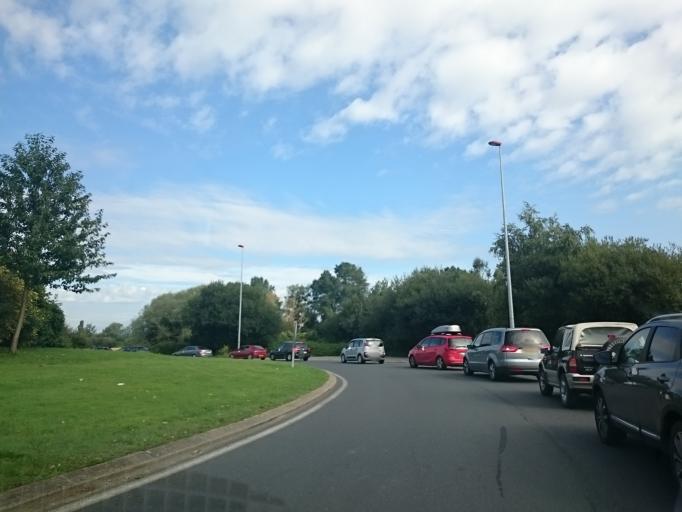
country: FR
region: Lower Normandy
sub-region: Departement de la Manche
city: Avranches
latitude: 48.6915
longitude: -1.3660
